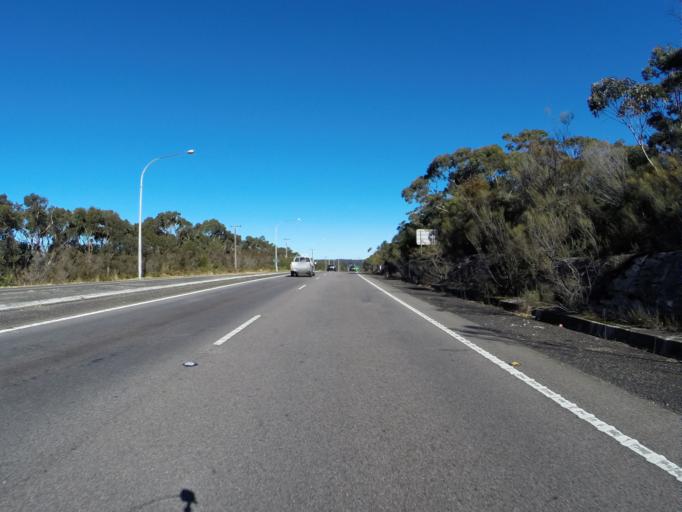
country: AU
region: New South Wales
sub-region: Wollongong
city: Bulli
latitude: -34.2989
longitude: 150.9147
